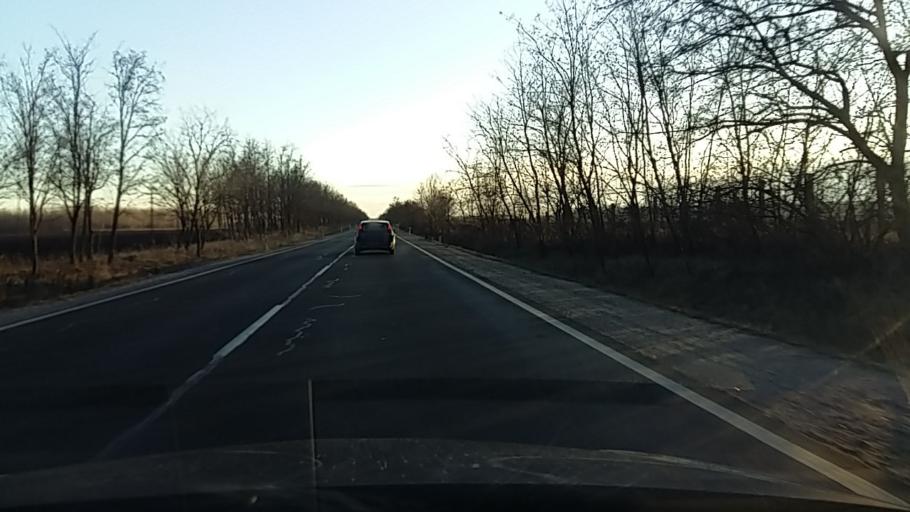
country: HU
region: Hajdu-Bihar
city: Teglas
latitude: 47.7499
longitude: 21.6774
